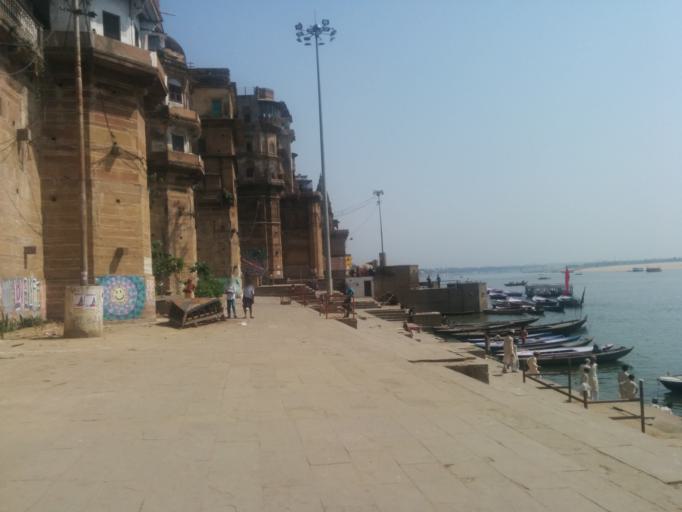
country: IN
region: Uttar Pradesh
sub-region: Varanasi
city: Varanasi
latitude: 25.3046
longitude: 83.0091
